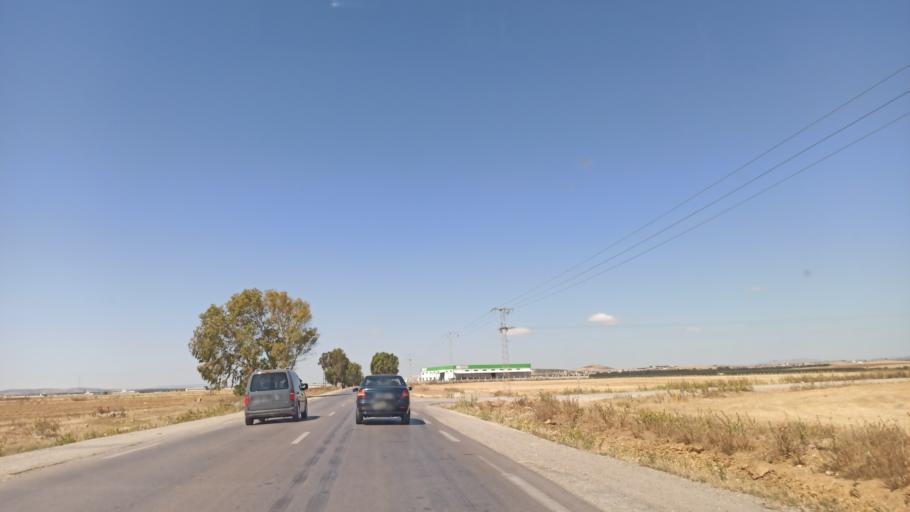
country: TN
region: Tunis
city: Oued Lill
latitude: 36.7411
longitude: 9.9558
